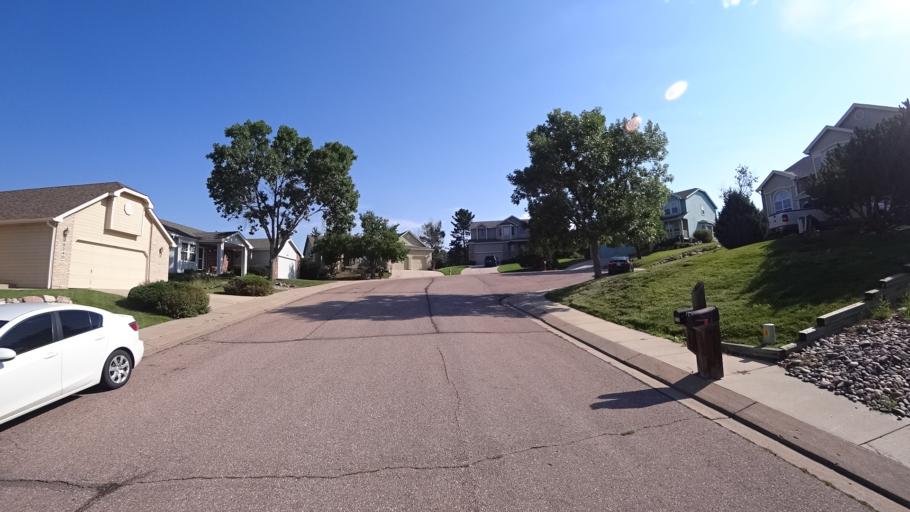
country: US
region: Colorado
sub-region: El Paso County
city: Air Force Academy
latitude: 38.9512
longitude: -104.7825
